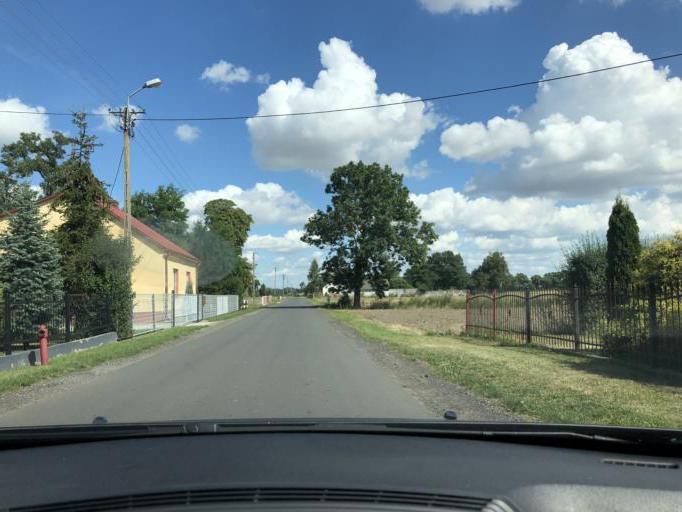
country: PL
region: Lodz Voivodeship
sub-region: Powiat wieruszowski
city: Czastary
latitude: 51.2376
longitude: 18.3576
